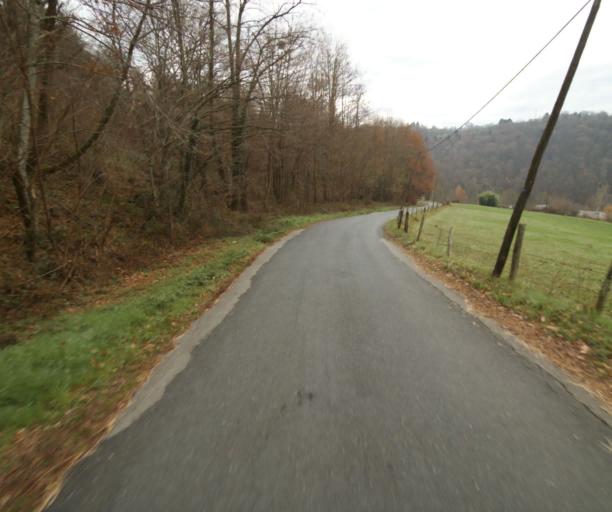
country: FR
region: Limousin
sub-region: Departement de la Correze
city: Tulle
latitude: 45.2446
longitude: 1.7383
